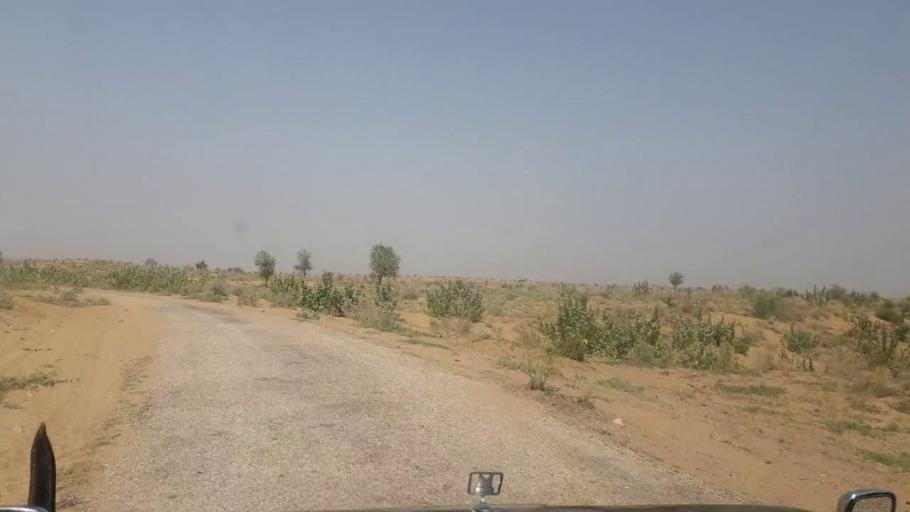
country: PK
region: Sindh
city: Islamkot
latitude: 25.1742
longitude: 70.2024
